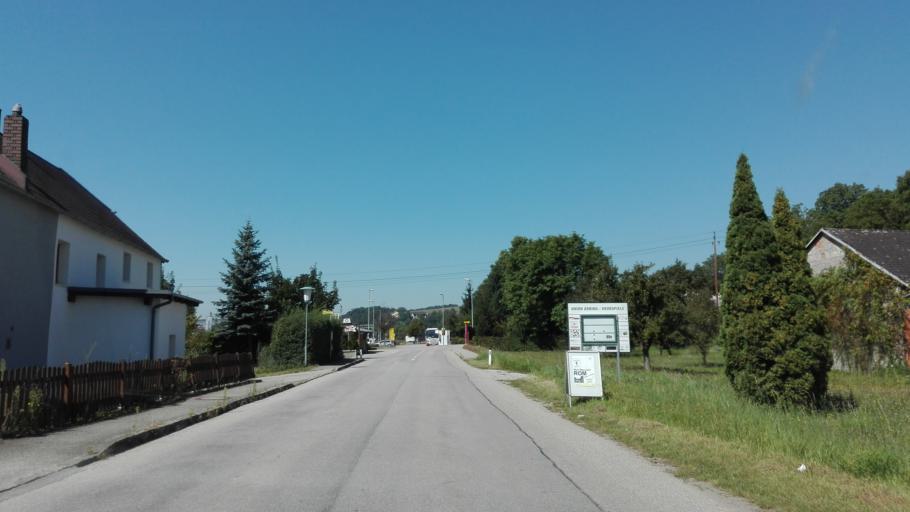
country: AT
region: Upper Austria
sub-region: Politischer Bezirk Perg
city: Perg
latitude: 48.2292
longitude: 14.7016
